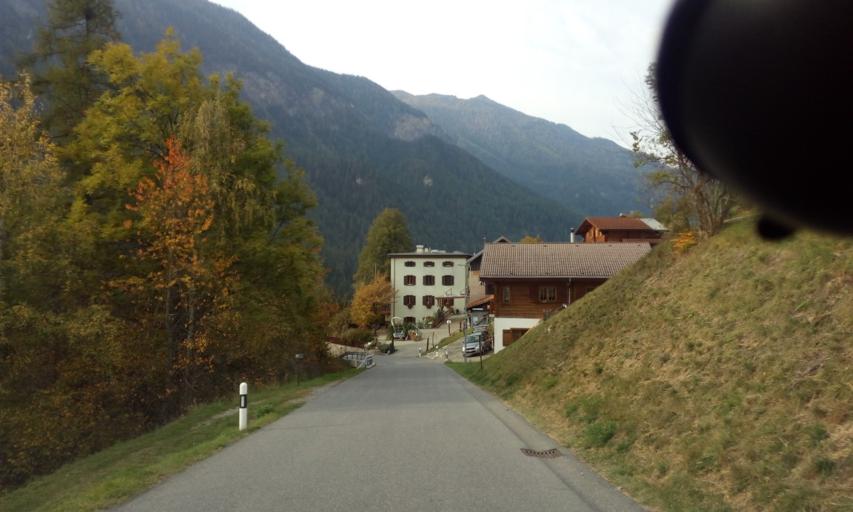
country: CH
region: Grisons
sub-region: Albula District
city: Tiefencastel
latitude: 46.6700
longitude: 9.6488
